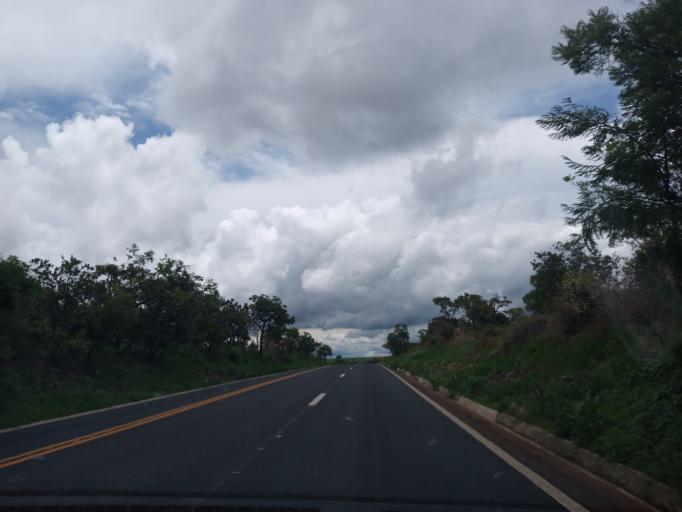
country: BR
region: Minas Gerais
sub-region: Uberaba
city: Uberaba
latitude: -19.2733
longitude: -47.6735
